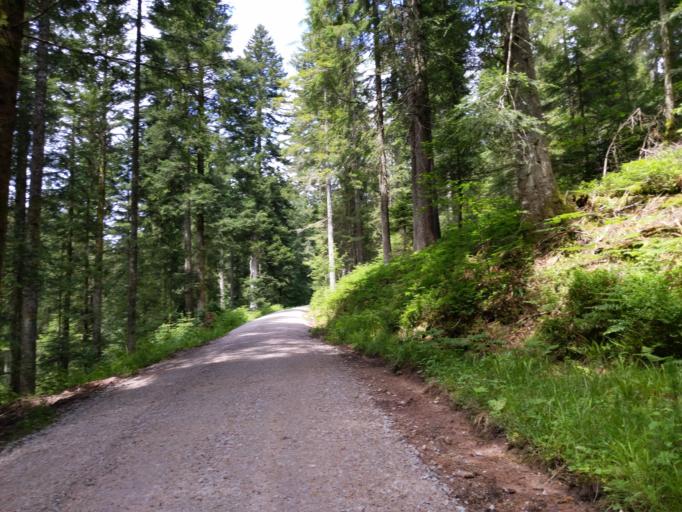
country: DE
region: Baden-Wuerttemberg
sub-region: Karlsruhe Region
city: Freudenstadt
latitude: 48.4404
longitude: 8.3710
